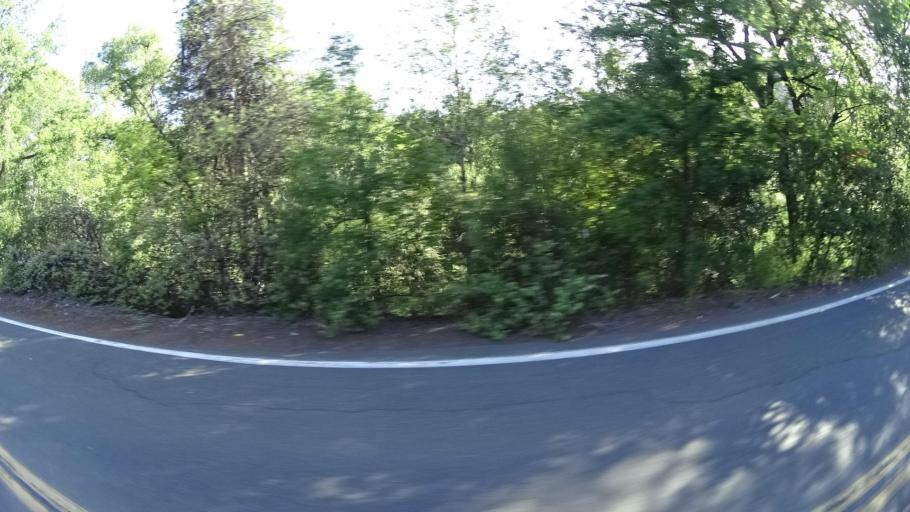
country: US
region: California
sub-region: Lake County
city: North Lakeport
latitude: 39.1112
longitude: -122.9777
